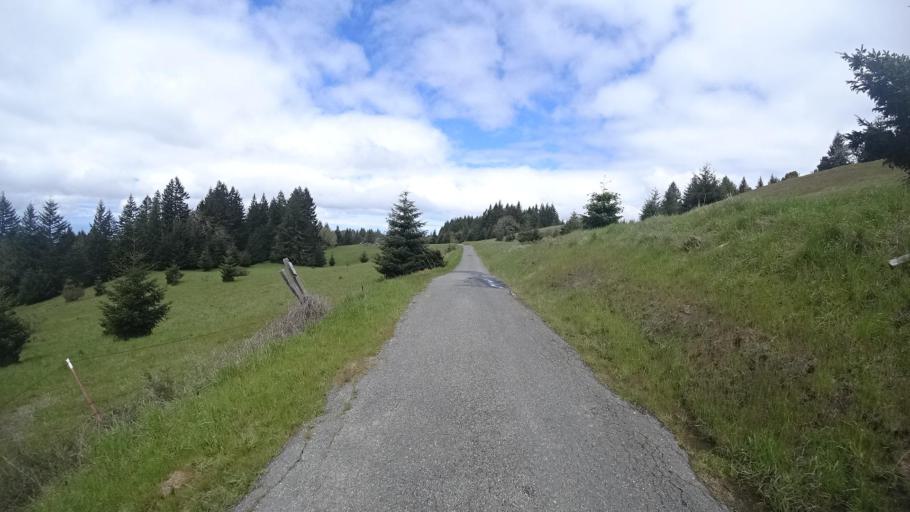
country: US
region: California
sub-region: Humboldt County
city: Blue Lake
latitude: 40.7889
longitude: -123.9667
